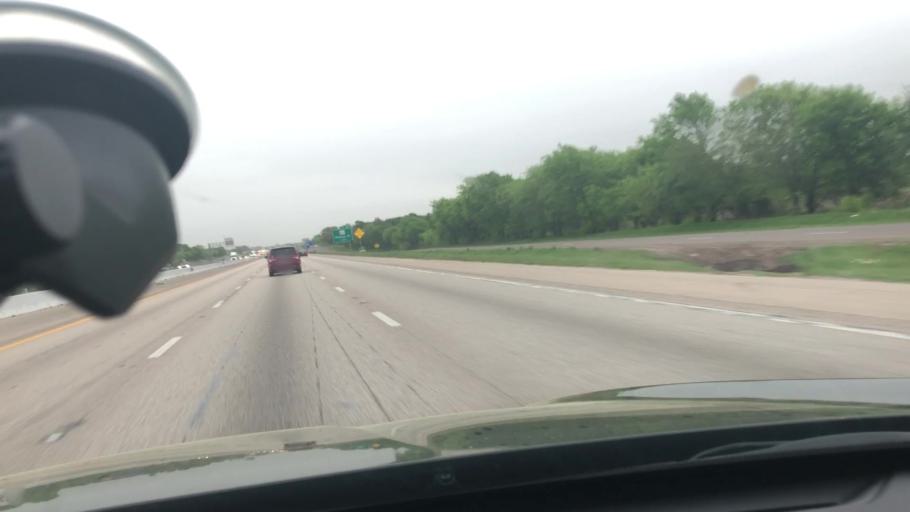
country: US
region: Texas
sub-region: Bell County
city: Belton
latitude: 31.0650
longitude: -97.4304
